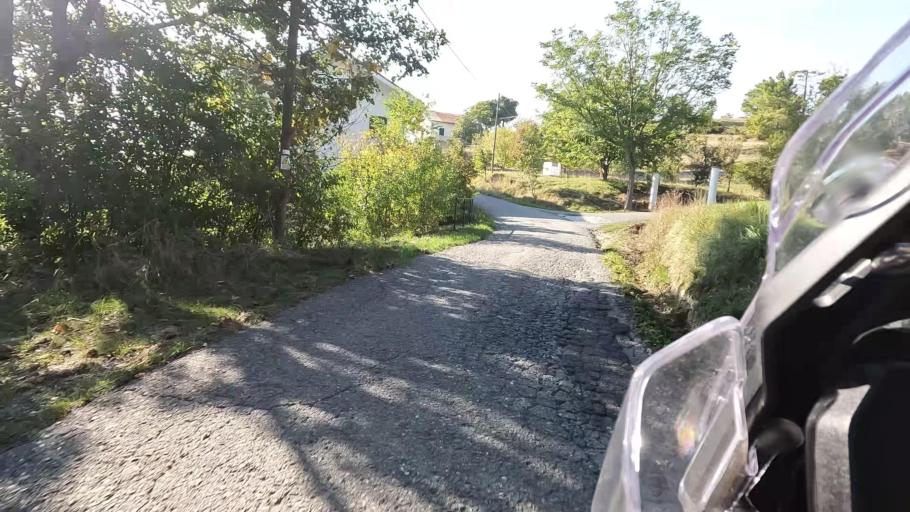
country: IT
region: Liguria
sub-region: Provincia di Savona
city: Urbe
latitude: 44.5285
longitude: 8.5457
